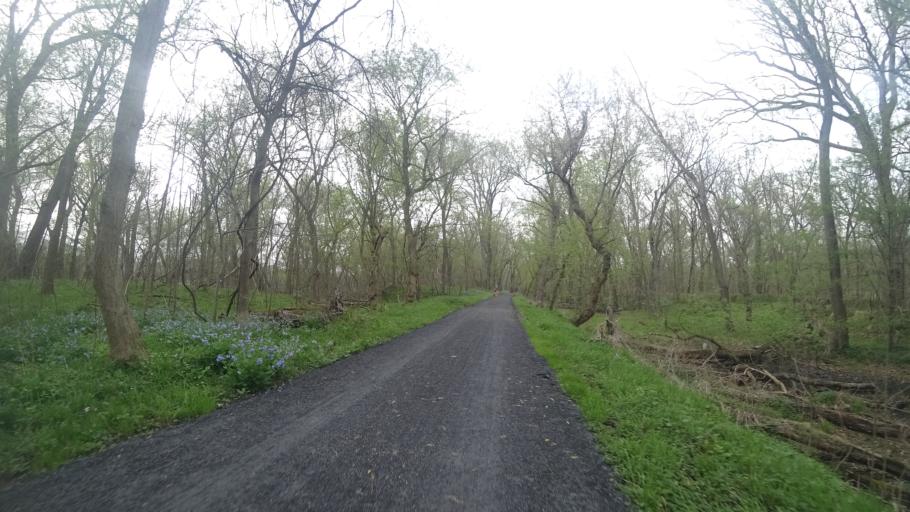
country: US
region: Virginia
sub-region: Loudoun County
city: University Center
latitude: 39.0902
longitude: -77.4635
